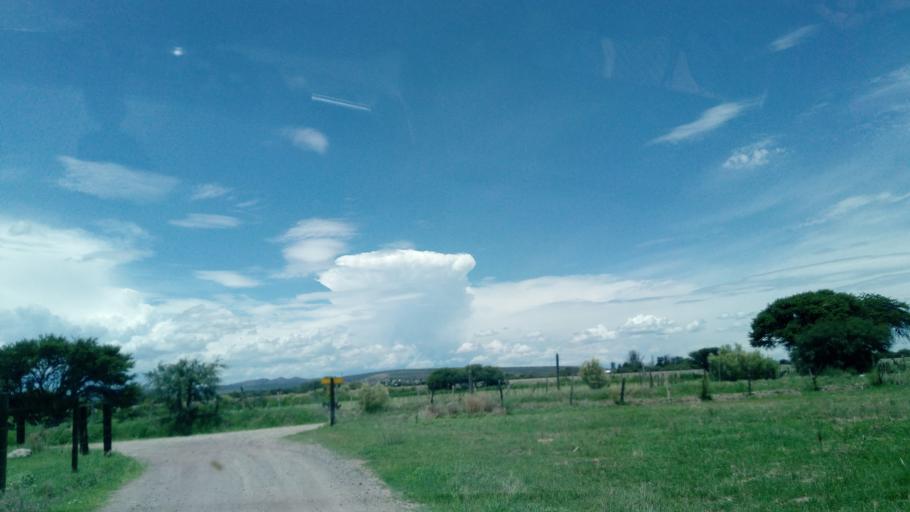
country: MX
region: Durango
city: Victoria de Durango
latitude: 24.0866
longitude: -104.5560
